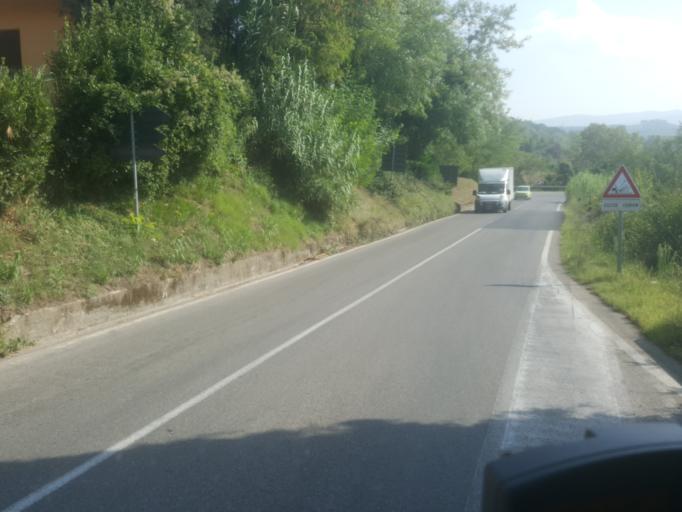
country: IT
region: Tuscany
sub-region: Province of Pisa
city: Peccioli
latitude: 43.5448
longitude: 10.7149
